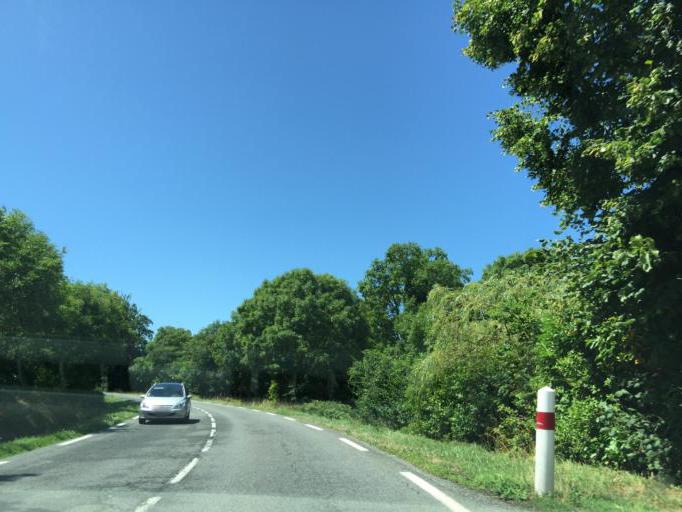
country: FR
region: Midi-Pyrenees
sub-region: Departement de l'Aveyron
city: Salles-Curan
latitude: 44.2426
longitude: 2.8940
